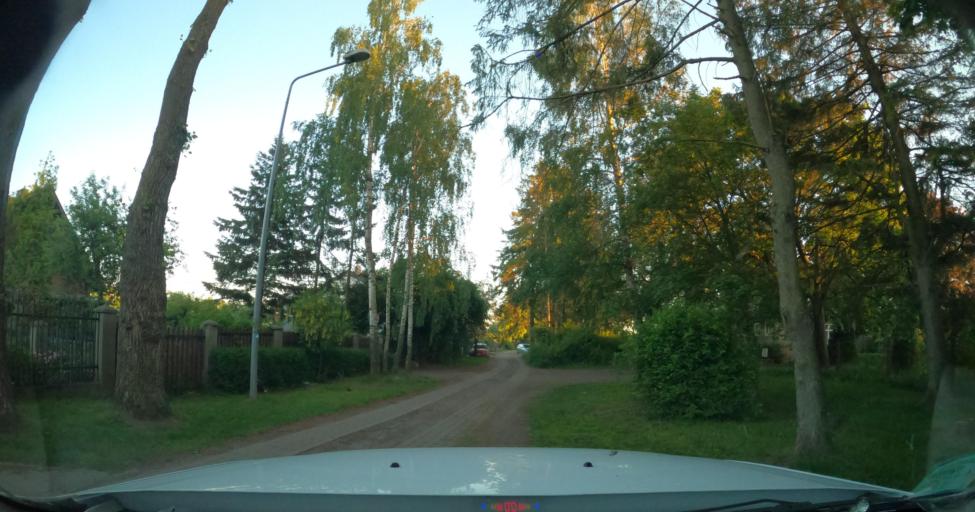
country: PL
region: Pomeranian Voivodeship
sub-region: Slupsk
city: Slupsk
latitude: 54.4718
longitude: 16.9988
